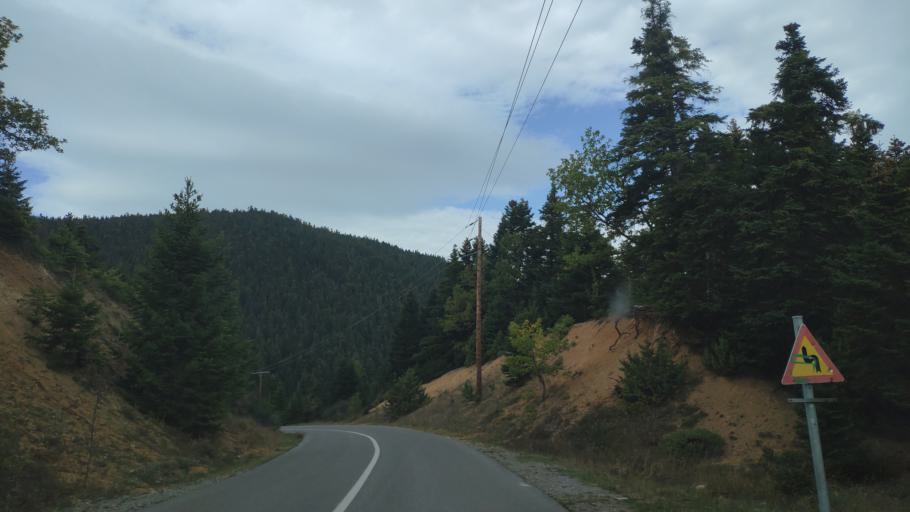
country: GR
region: Central Greece
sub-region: Nomos Fokidos
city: Amfissa
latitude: 38.7080
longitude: 22.3263
